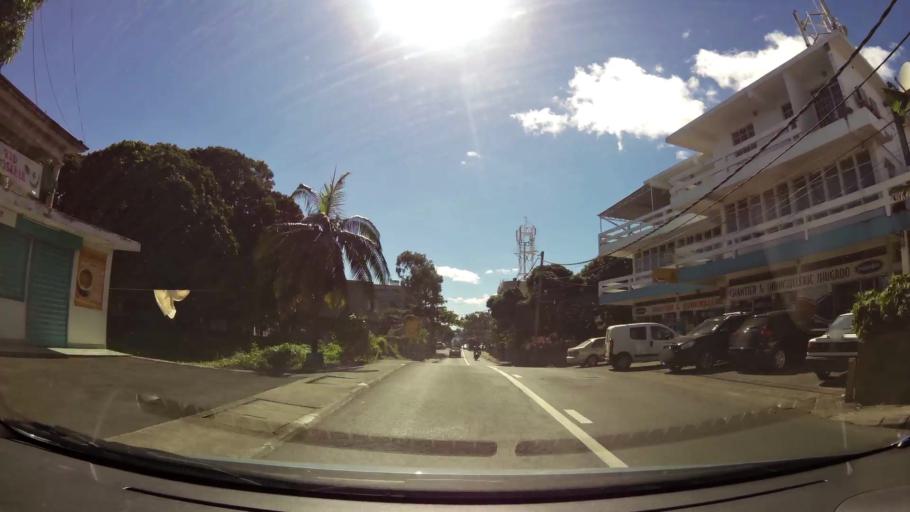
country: MU
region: Plaines Wilhems
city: Vacoas
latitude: -20.3141
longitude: 57.4849
